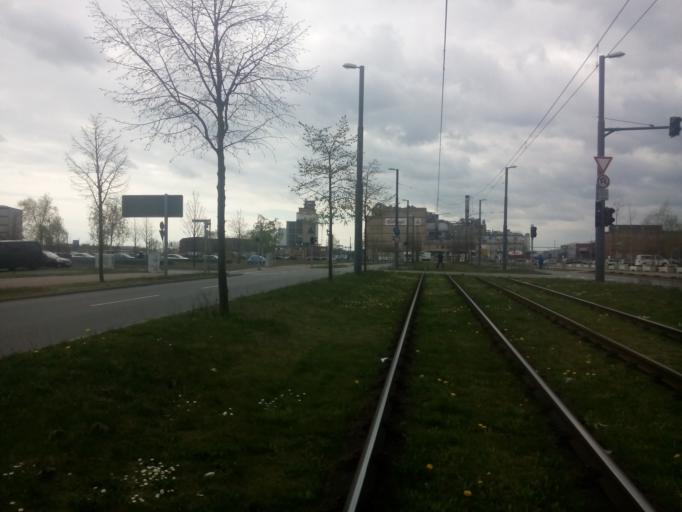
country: DE
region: Bremen
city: Bremen
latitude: 53.0865
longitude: 8.7819
